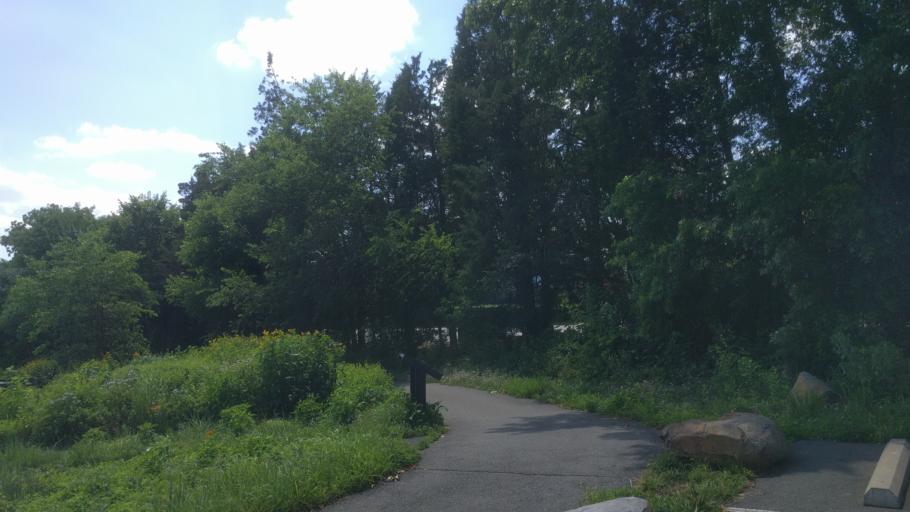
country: US
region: Virginia
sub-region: Fairfax County
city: Floris
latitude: 38.9531
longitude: -77.4111
